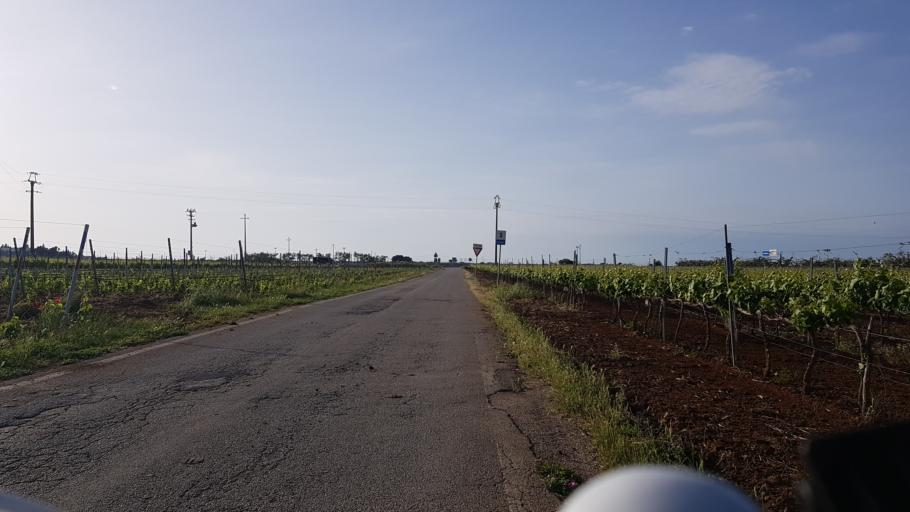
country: IT
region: Apulia
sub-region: Provincia di Brindisi
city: Mesagne
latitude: 40.5871
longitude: 17.8572
